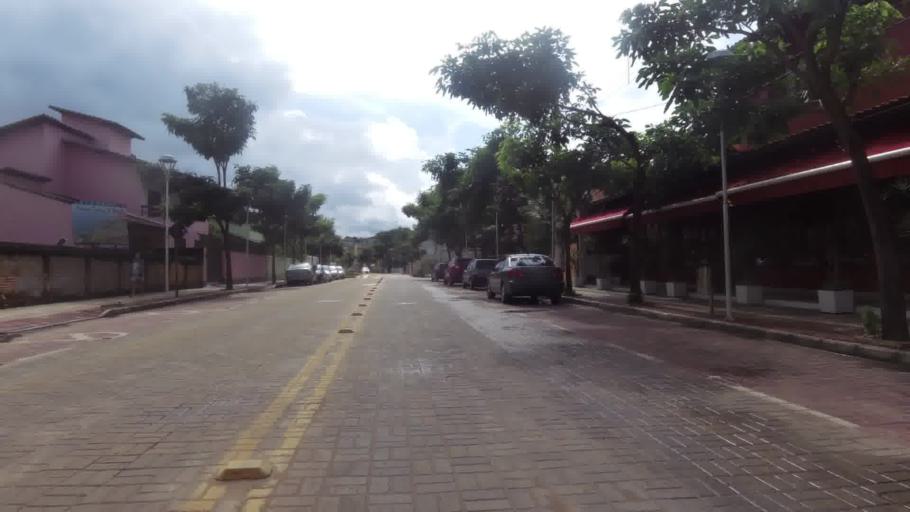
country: BR
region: Espirito Santo
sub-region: Piuma
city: Piuma
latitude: -20.8296
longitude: -40.6932
